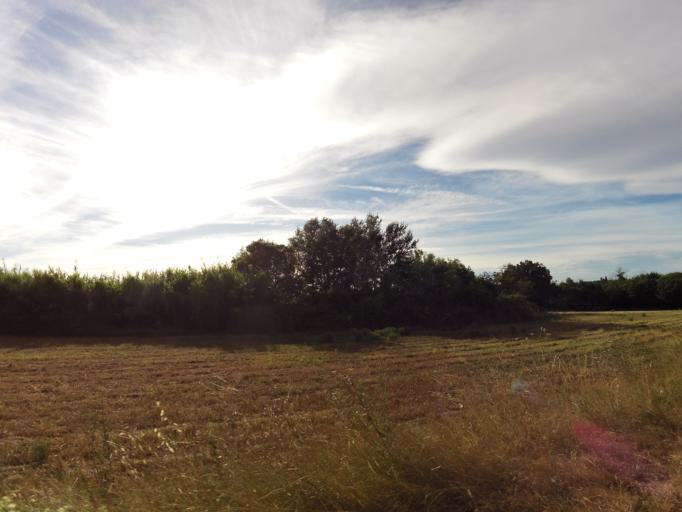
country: FR
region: Languedoc-Roussillon
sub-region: Departement du Gard
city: Congenies
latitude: 43.8168
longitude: 4.1475
